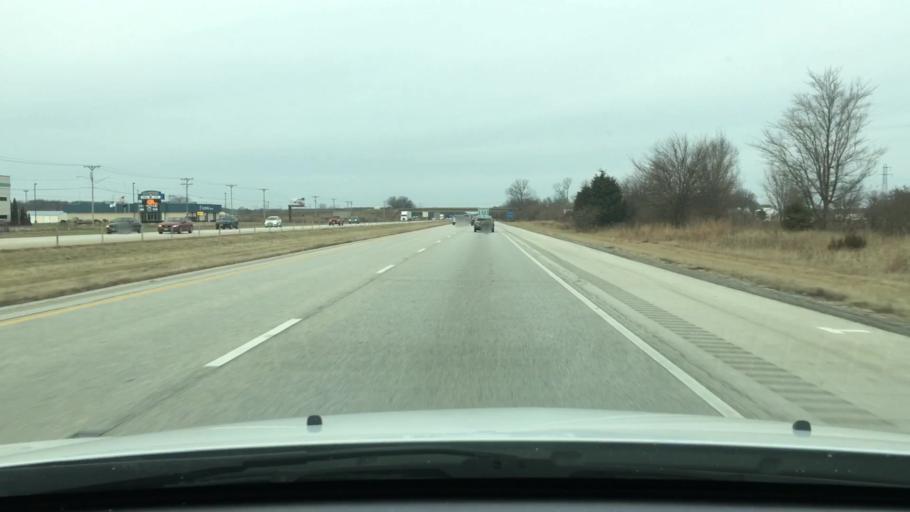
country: US
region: Illinois
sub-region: Sangamon County
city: Grandview
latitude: 39.8411
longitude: -89.5937
